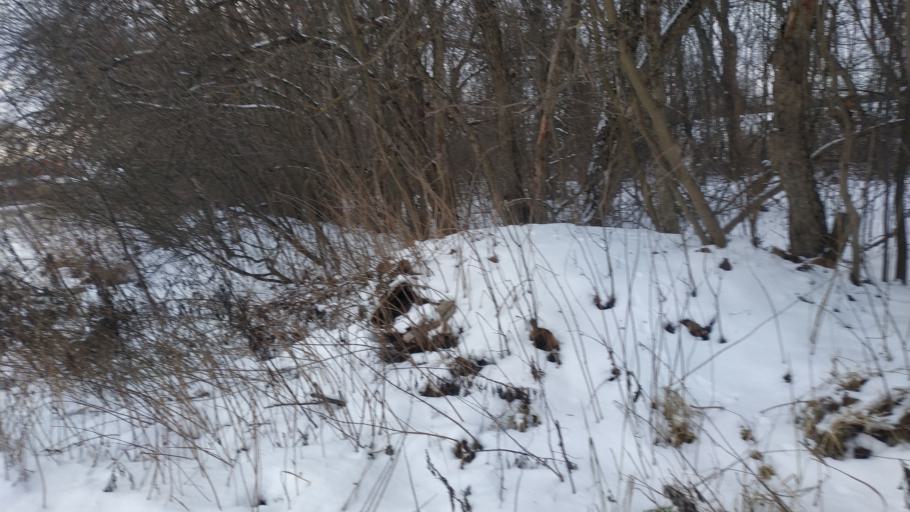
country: RU
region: Moskovskaya
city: Svatkovo
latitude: 56.3918
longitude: 38.2982
